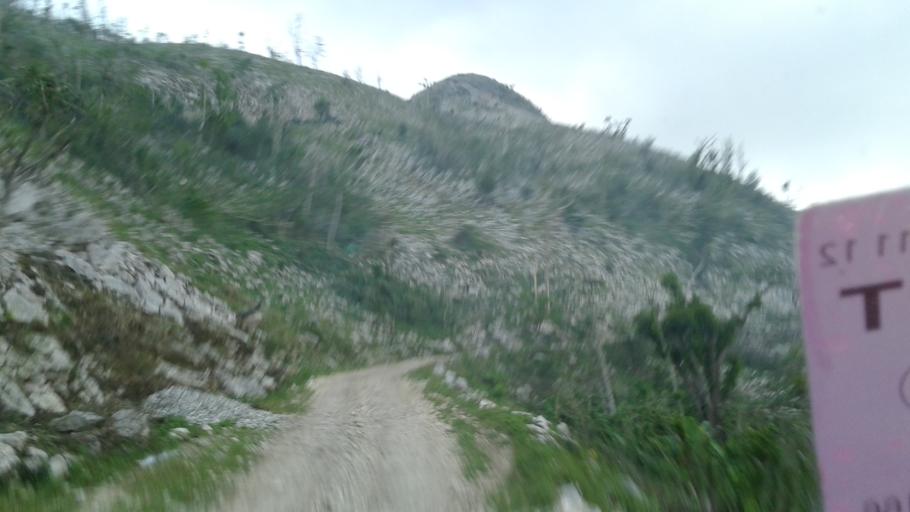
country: HT
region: Grandans
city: Jeremie
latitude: 18.4982
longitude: -74.0973
